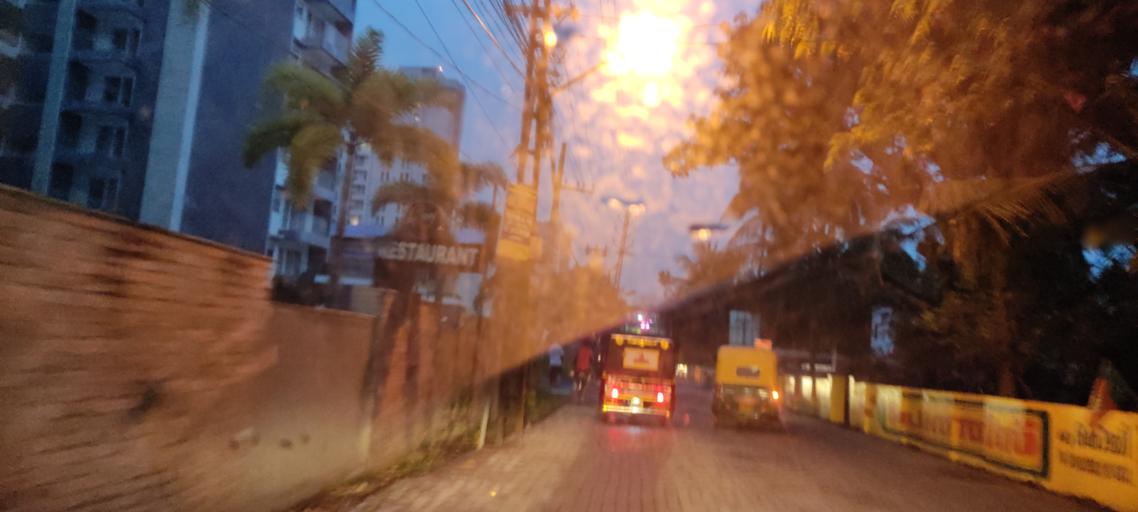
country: IN
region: Kerala
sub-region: Ernakulam
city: Cochin
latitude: 9.9019
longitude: 76.2951
